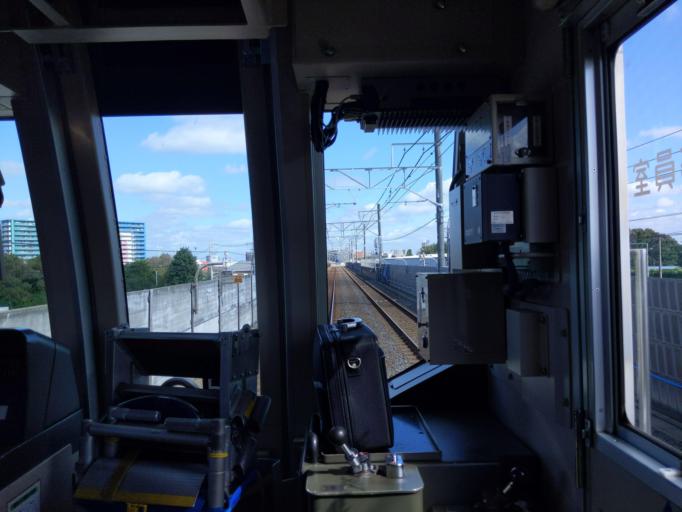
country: JP
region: Chiba
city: Shiroi
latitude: 35.7298
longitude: 140.0857
